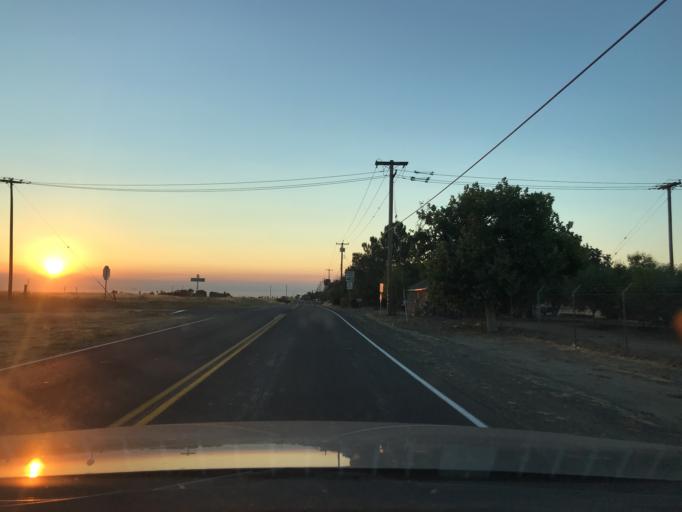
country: US
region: California
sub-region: Merced County
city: Merced
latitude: 37.3390
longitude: -120.5233
